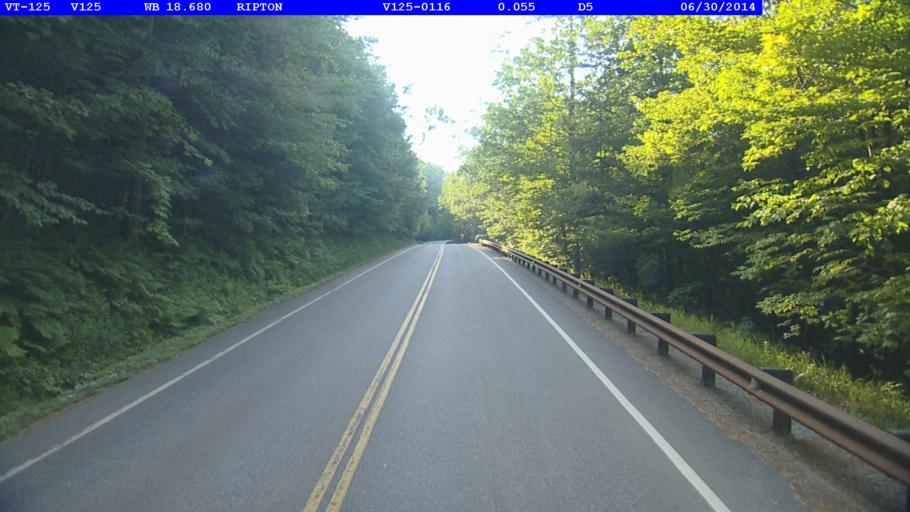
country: US
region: Vermont
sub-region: Addison County
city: Middlebury (village)
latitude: 43.9723
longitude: -73.0580
